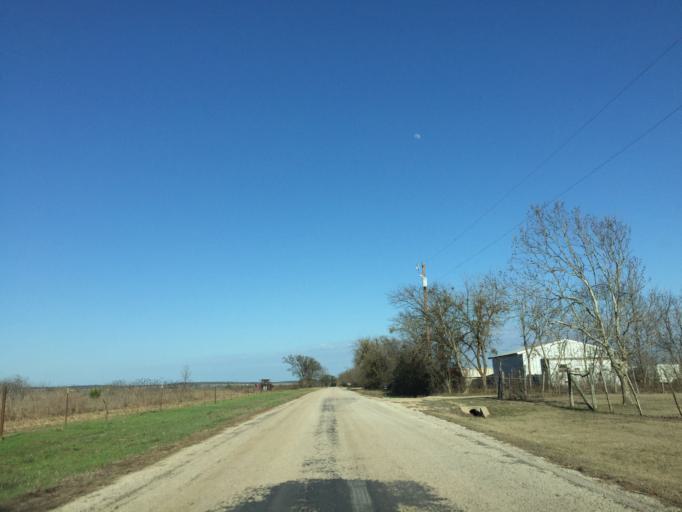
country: US
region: Texas
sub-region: Williamson County
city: Florence
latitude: 30.7751
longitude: -97.8466
